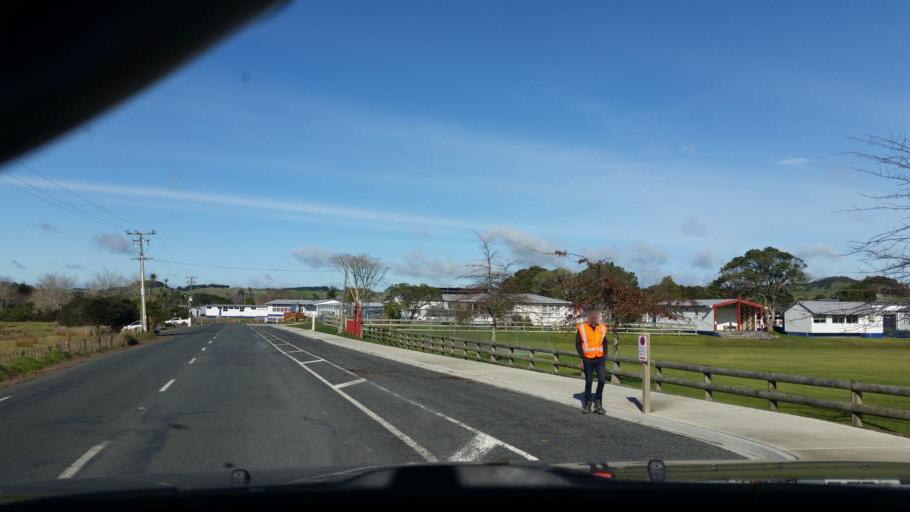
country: NZ
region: Northland
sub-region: Whangarei
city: Ruakaka
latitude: -36.1152
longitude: 174.3654
